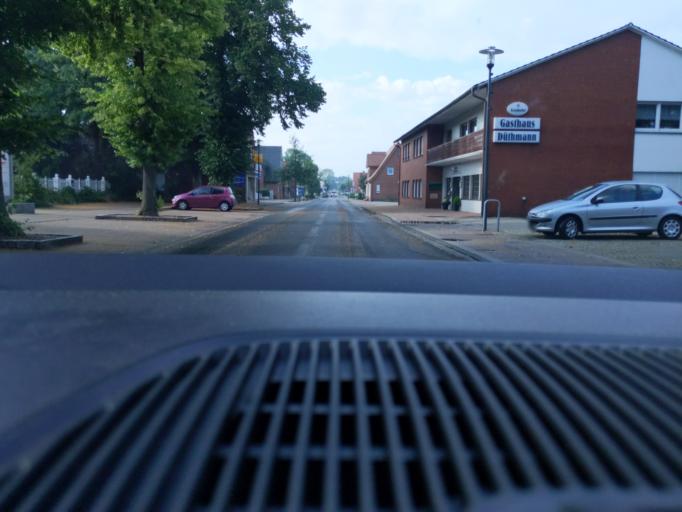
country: NL
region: Drenthe
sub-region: Gemeente Emmen
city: Emmer-Compascuum
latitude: 52.8387
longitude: 7.1013
